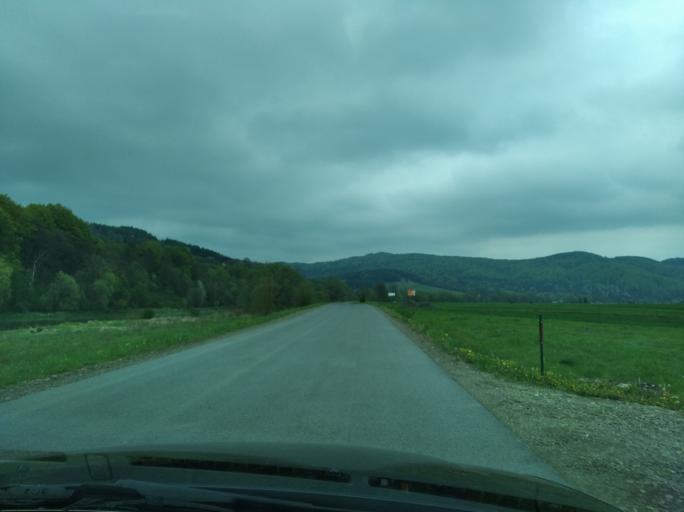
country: PL
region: Subcarpathian Voivodeship
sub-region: Powiat sanocki
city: Sanok
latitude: 49.6069
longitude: 22.2350
